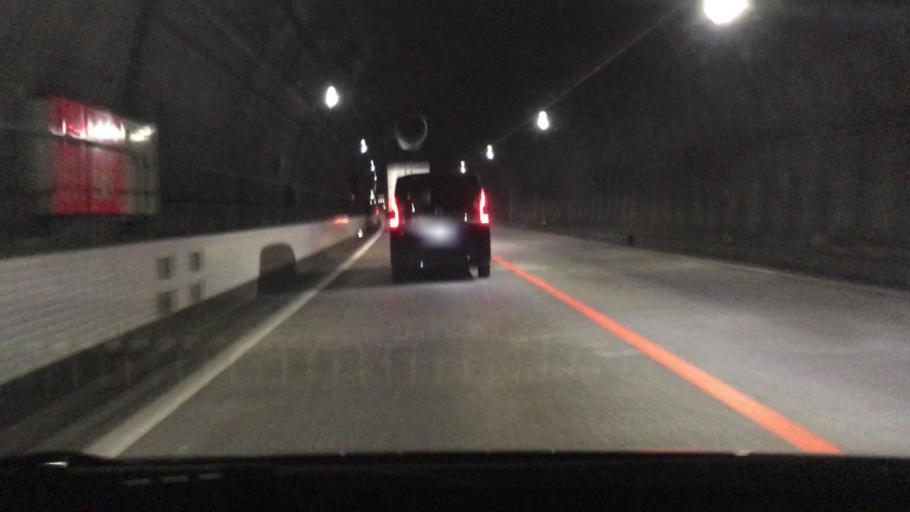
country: JP
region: Yamaguchi
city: Otake
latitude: 34.2097
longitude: 132.1814
